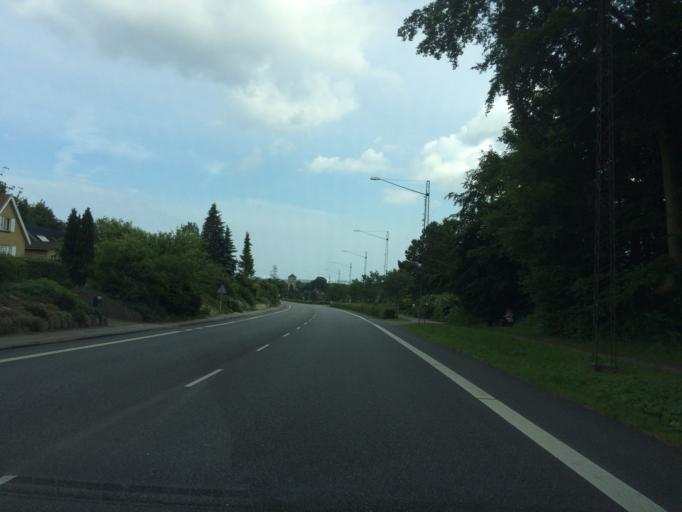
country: DK
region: South Denmark
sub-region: Middelfart Kommune
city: Middelfart
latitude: 55.5012
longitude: 9.7143
